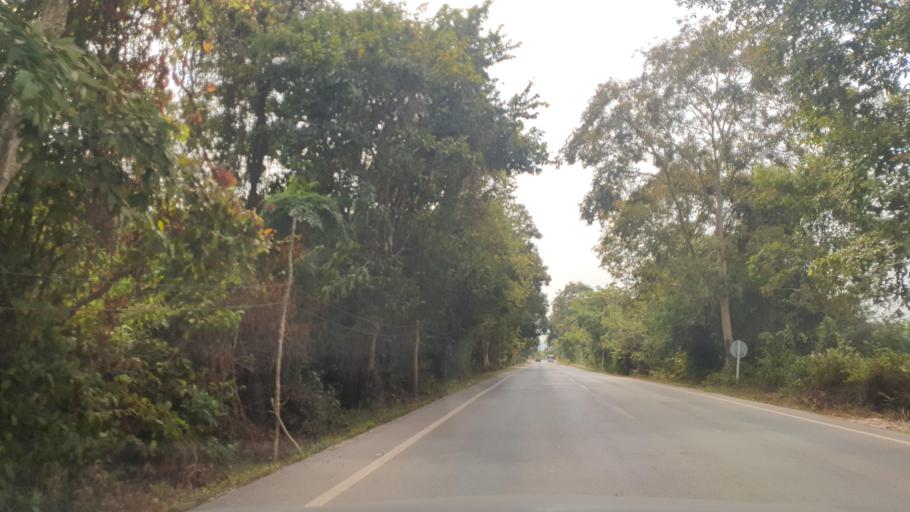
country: TH
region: Changwat Bueng Kan
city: Bung Khla
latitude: 18.2882
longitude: 103.8860
